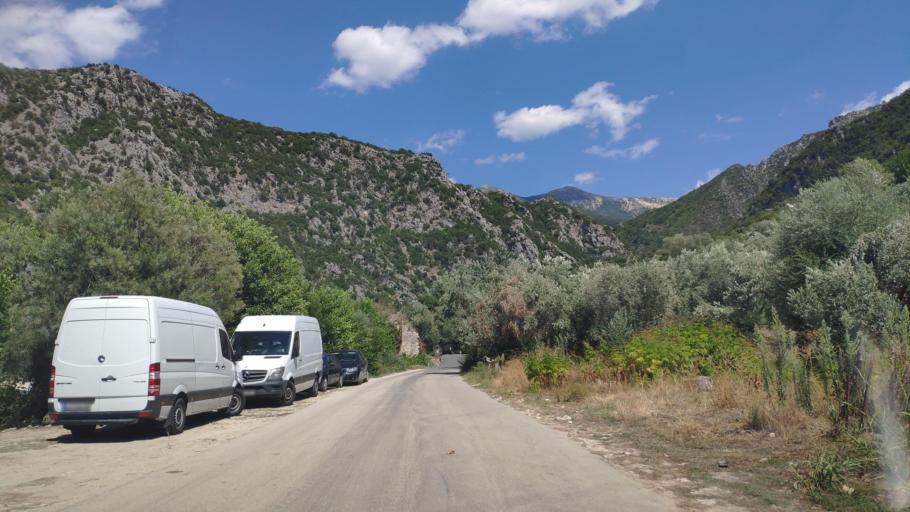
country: GR
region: Epirus
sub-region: Nomos Prevezis
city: Kanalaki
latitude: 39.3266
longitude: 20.6176
